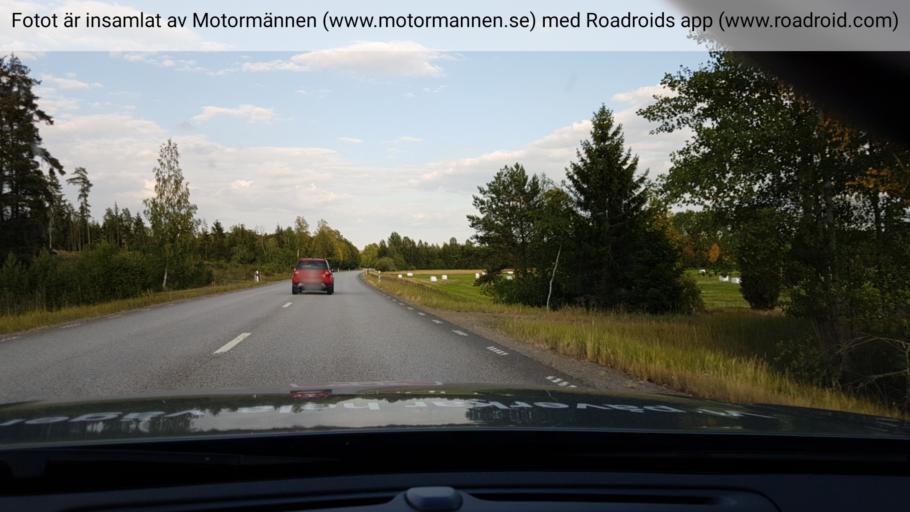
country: SE
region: Uppsala
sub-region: Enkopings Kommun
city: Orsundsbro
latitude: 59.8912
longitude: 17.1655
